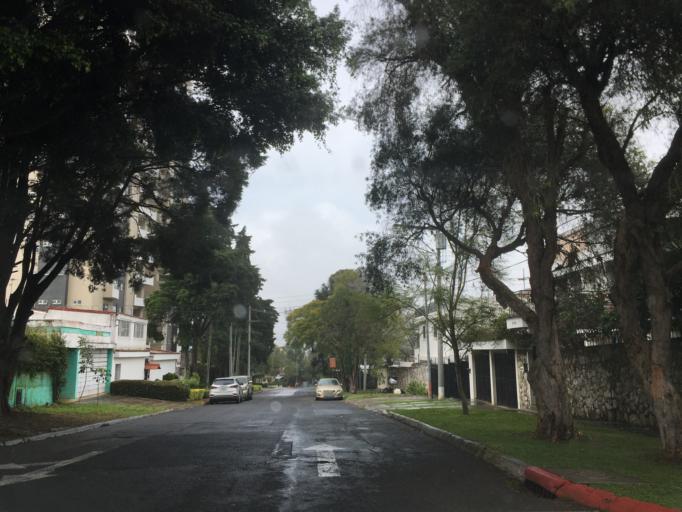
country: GT
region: Guatemala
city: Santa Catarina Pinula
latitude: 14.5872
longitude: -90.4942
